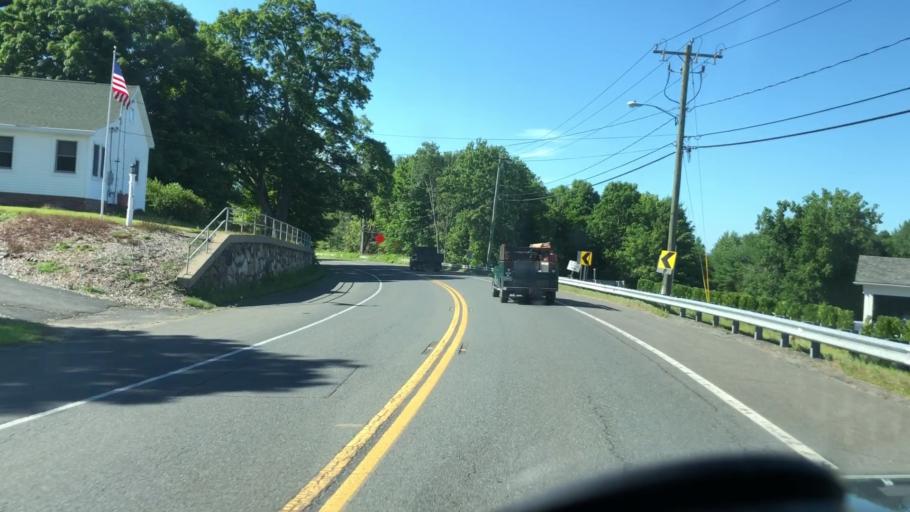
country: US
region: Massachusetts
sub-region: Hampshire County
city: Southampton
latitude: 42.2094
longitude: -72.7258
